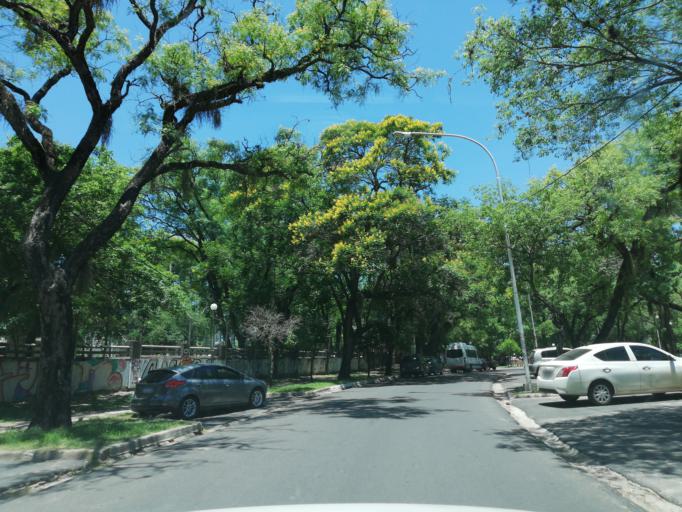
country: AR
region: Corrientes
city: Corrientes
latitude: -27.4588
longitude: -58.8279
